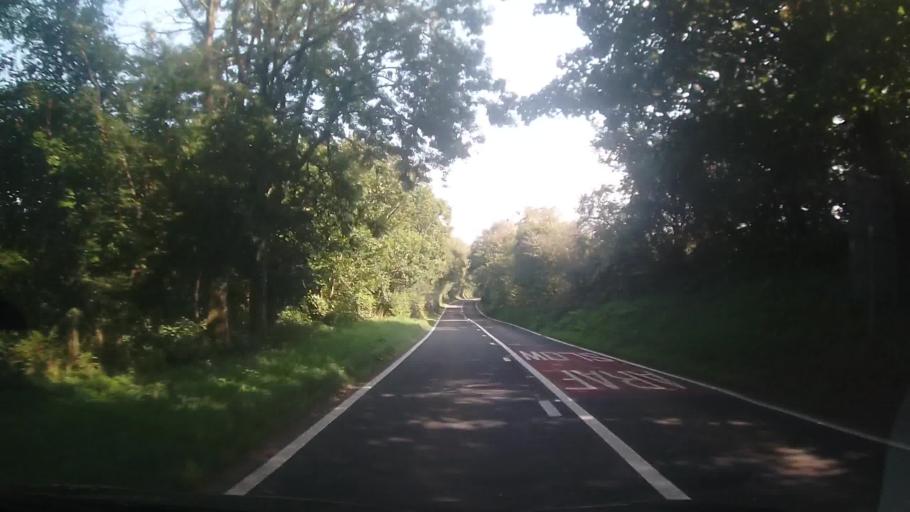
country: GB
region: Wales
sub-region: Pembrokeshire
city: Nevern
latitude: 52.0175
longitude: -4.7923
